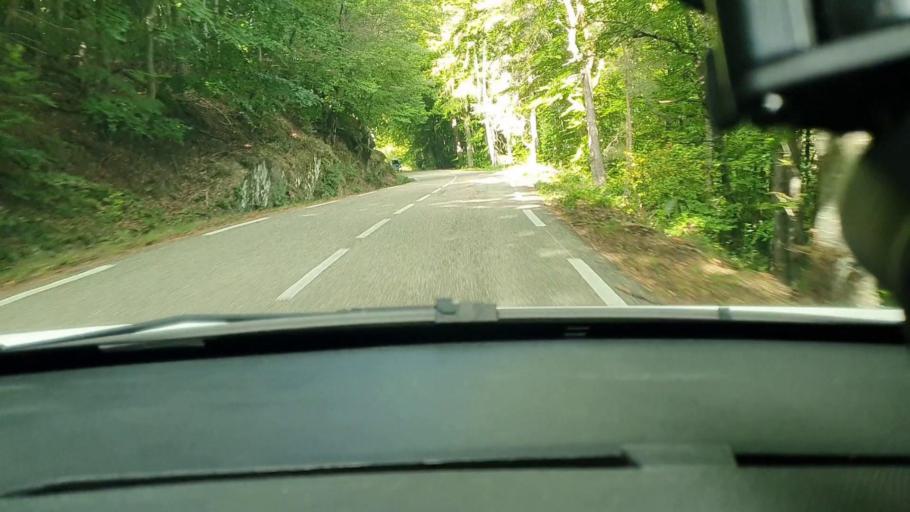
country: FR
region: Rhone-Alpes
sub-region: Departement de l'Ardeche
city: Les Vans
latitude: 44.4298
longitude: 3.9997
